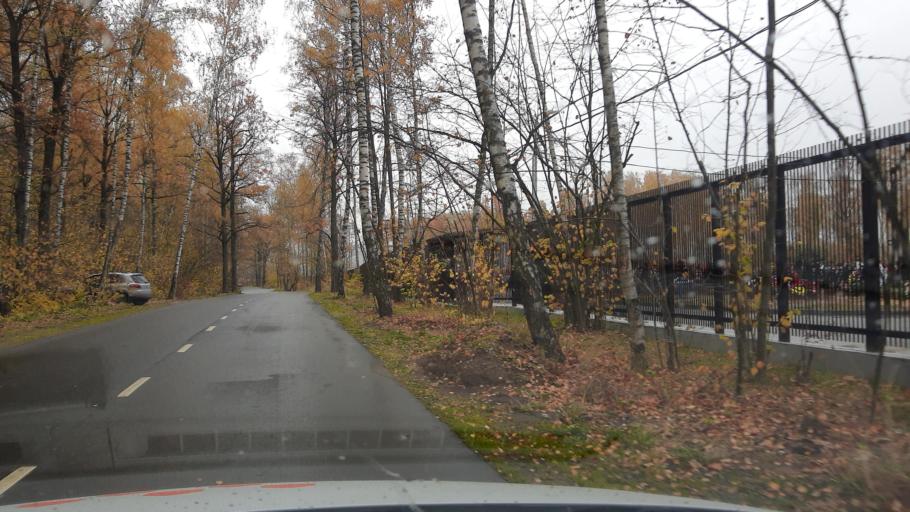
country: RU
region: Moskovskaya
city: Shcherbinka
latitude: 55.5298
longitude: 37.5631
